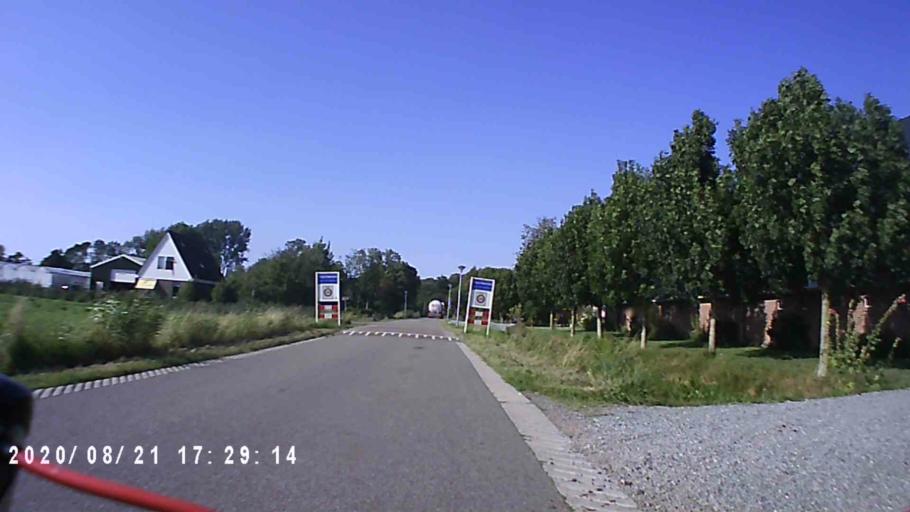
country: NL
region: Groningen
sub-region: Gemeente Bedum
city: Bedum
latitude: 53.2695
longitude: 6.5891
